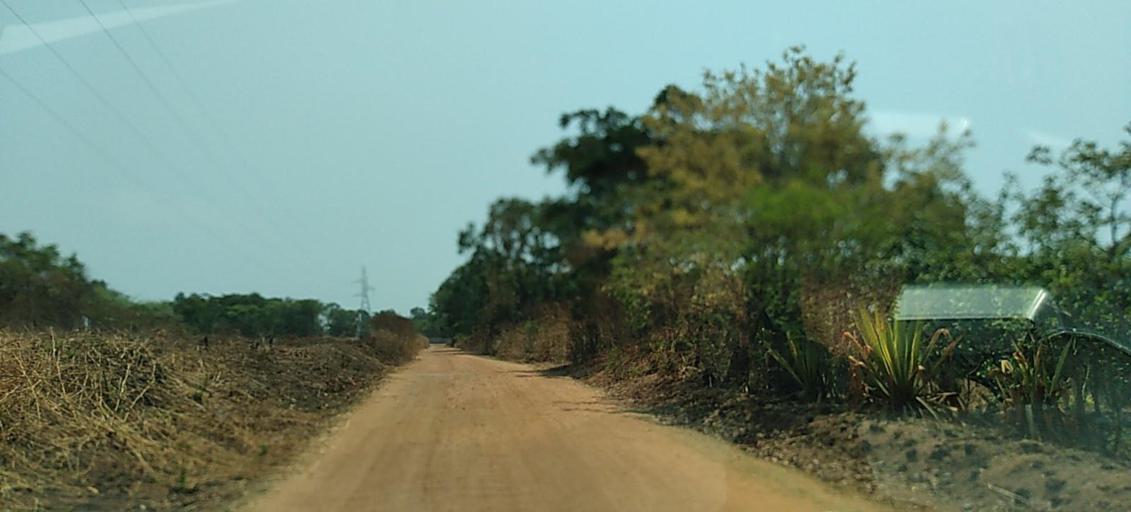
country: ZM
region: Copperbelt
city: Chambishi
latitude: -12.6194
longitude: 27.9478
